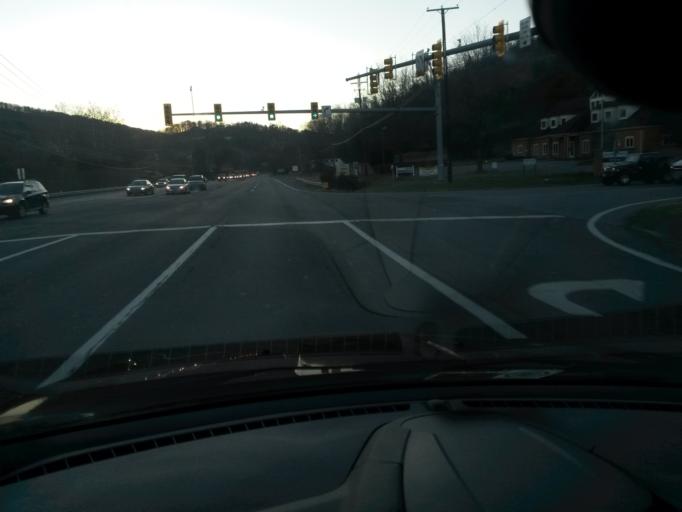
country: US
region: Virginia
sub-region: Roanoke County
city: Narrows
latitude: 37.2033
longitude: -79.9500
